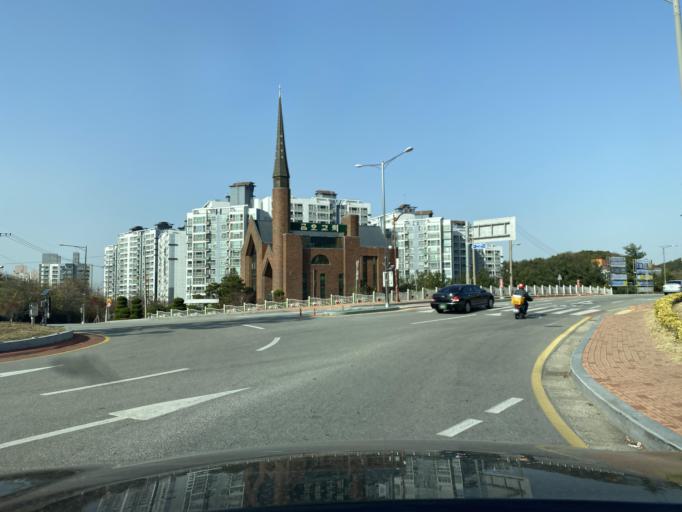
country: KR
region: Chungcheongnam-do
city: Yesan
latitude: 36.6868
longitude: 126.8433
